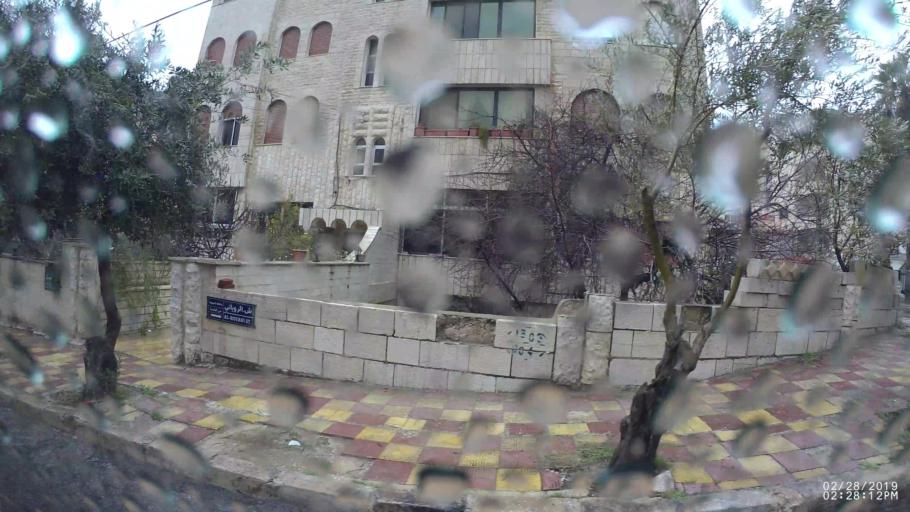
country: JO
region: Amman
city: Al Jubayhah
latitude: 32.0230
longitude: 35.8628
